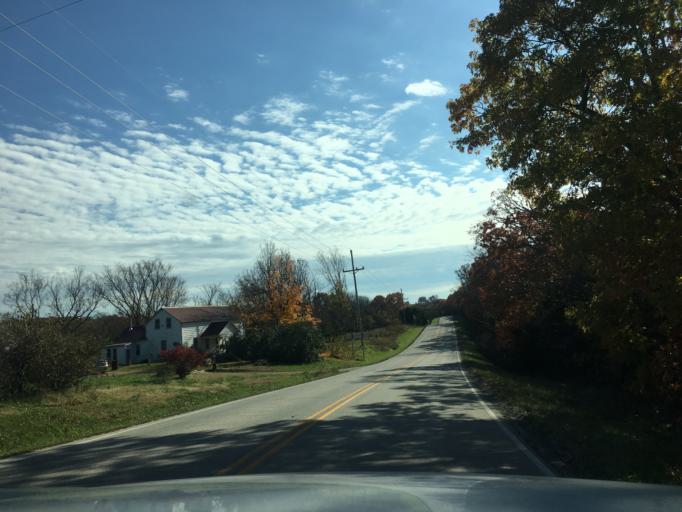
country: US
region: Missouri
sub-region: Maries County
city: Belle
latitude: 38.3359
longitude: -91.7627
